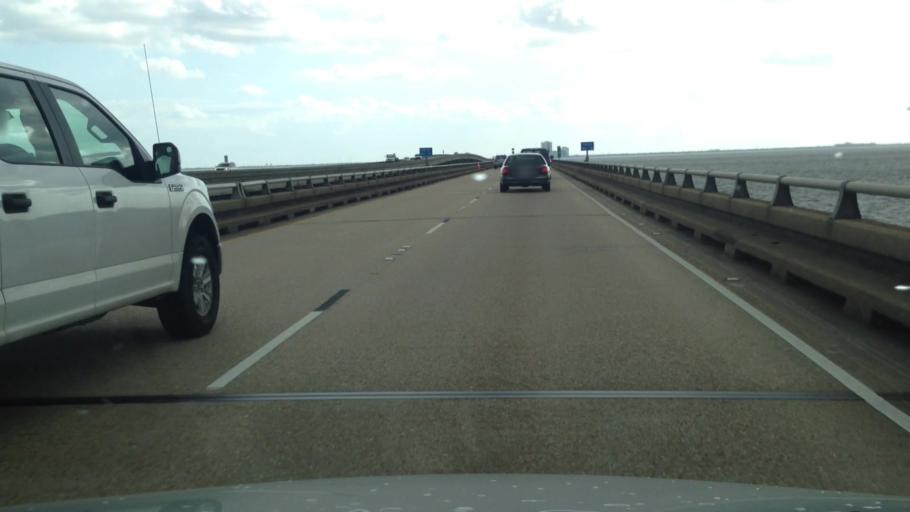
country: US
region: Louisiana
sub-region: Jefferson Parish
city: Metairie
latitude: 30.0817
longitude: -90.1436
